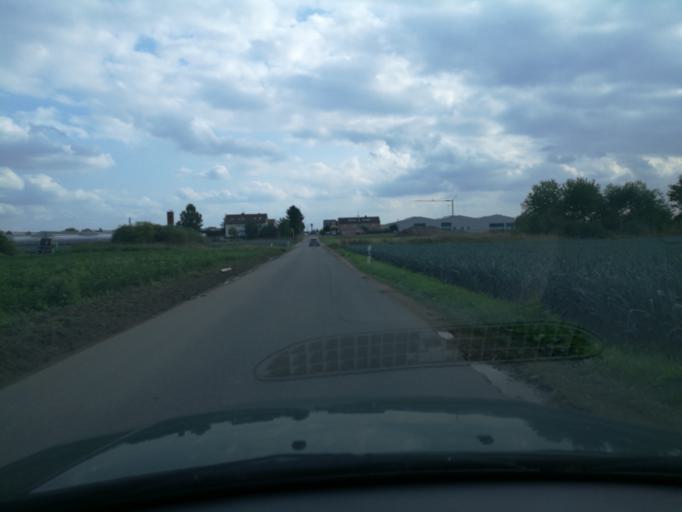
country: DE
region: Bavaria
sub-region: Regierungsbezirk Mittelfranken
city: Wetzendorf
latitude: 49.4824
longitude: 11.0290
